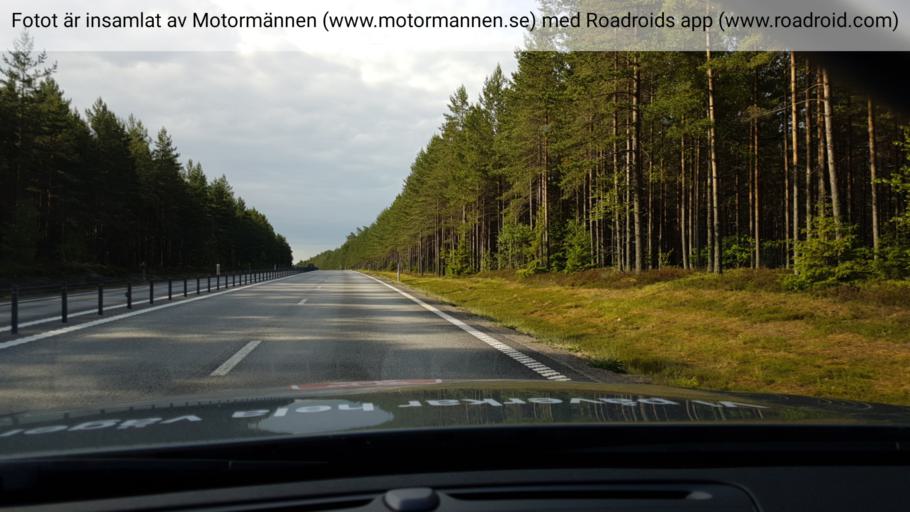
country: SE
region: OErebro
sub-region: Askersunds Kommun
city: Asbro
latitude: 59.0354
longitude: 15.0229
